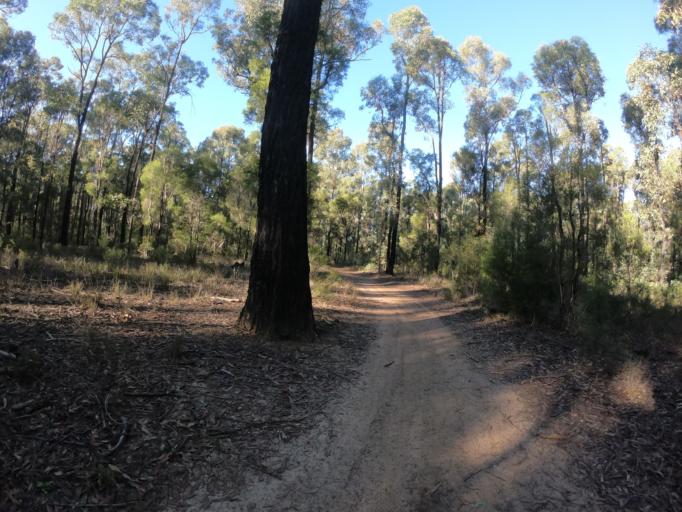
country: AU
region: New South Wales
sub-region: Hawkesbury
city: South Windsor
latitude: -33.6448
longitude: 150.7972
